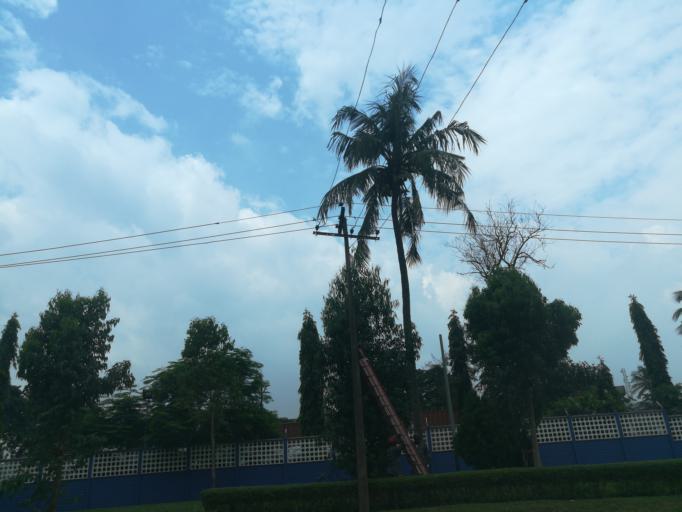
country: NG
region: Lagos
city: Ojota
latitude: 6.6032
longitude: 3.3691
